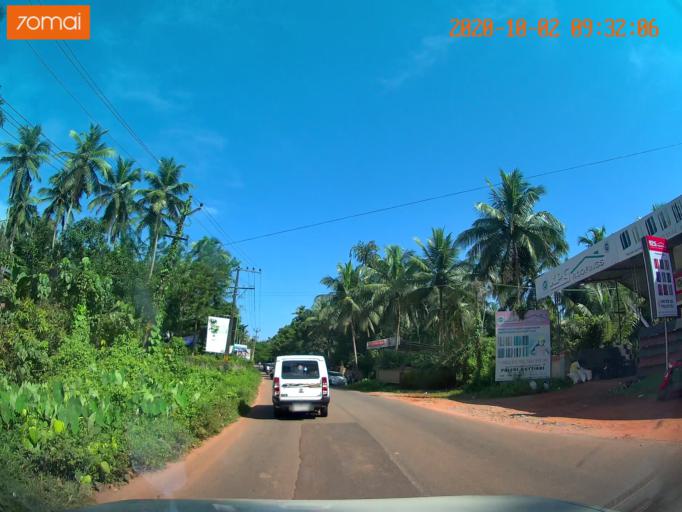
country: IN
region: Kerala
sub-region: Kozhikode
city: Nadapuram
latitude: 11.6261
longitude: 75.7573
